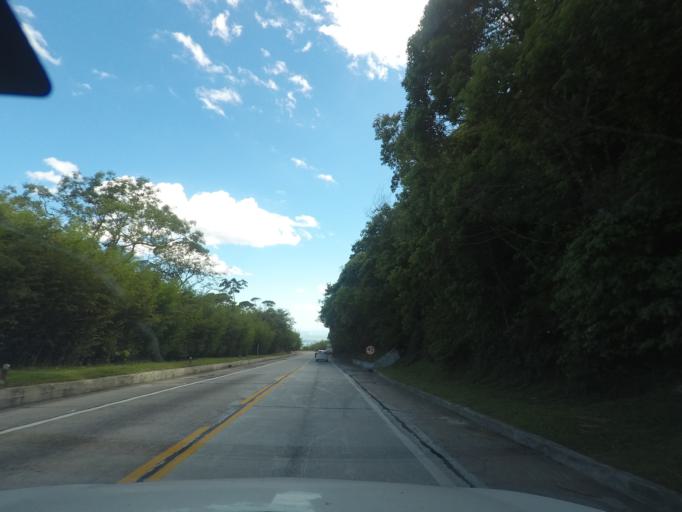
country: BR
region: Rio de Janeiro
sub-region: Guapimirim
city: Guapimirim
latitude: -22.4786
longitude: -42.9976
